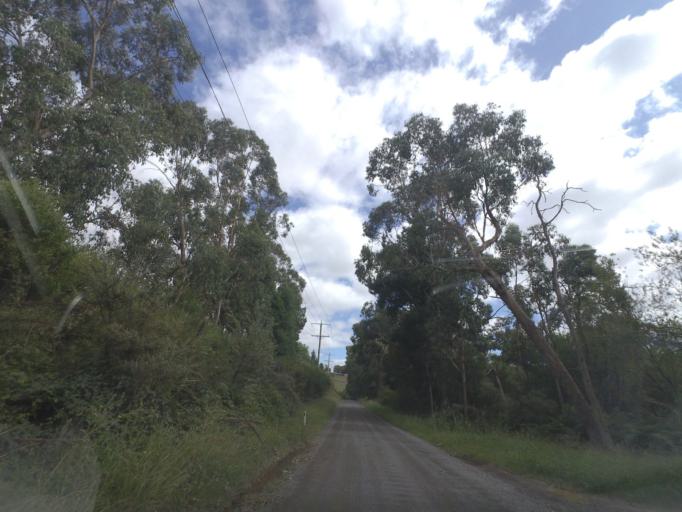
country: AU
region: Victoria
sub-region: Yarra Ranges
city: Mount Evelyn
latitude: -37.7880
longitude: 145.4100
